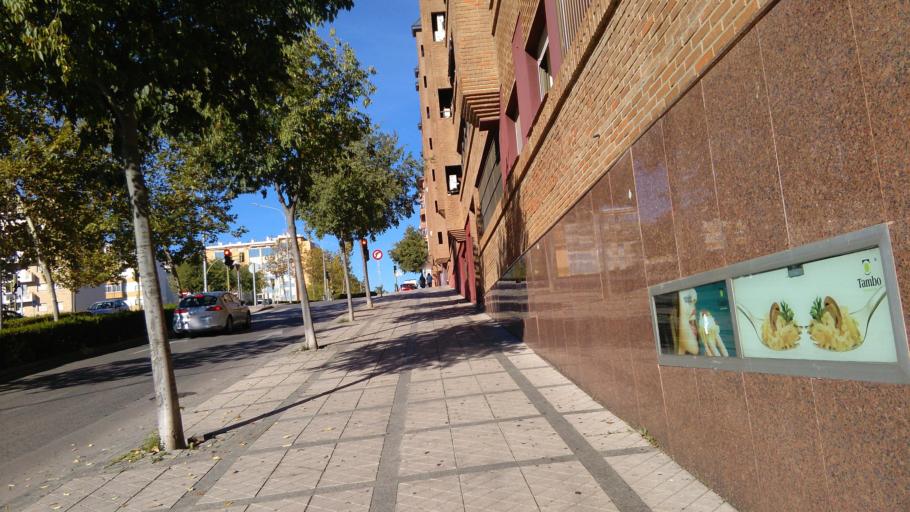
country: ES
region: Extremadura
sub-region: Provincia de Caceres
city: Caceres
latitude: 39.4658
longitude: -6.3814
